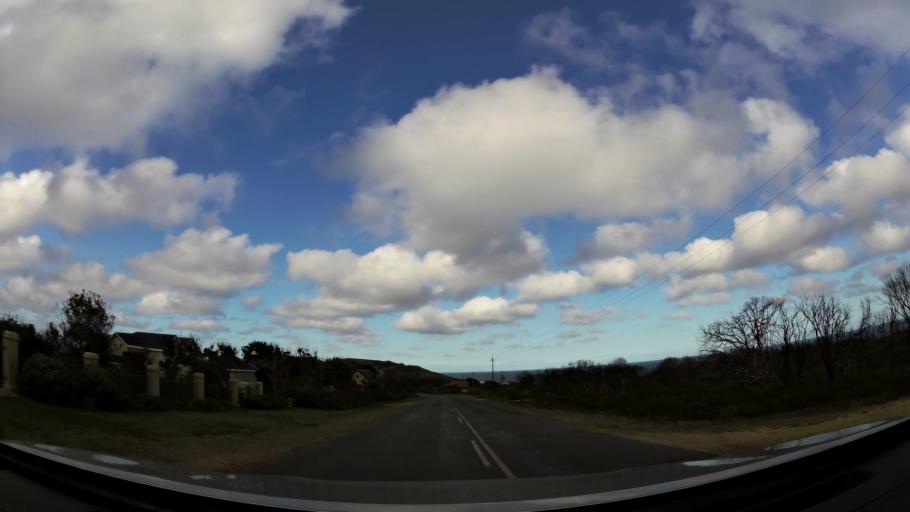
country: ZA
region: Western Cape
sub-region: Eden District Municipality
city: Plettenberg Bay
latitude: -34.0976
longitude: 23.3686
